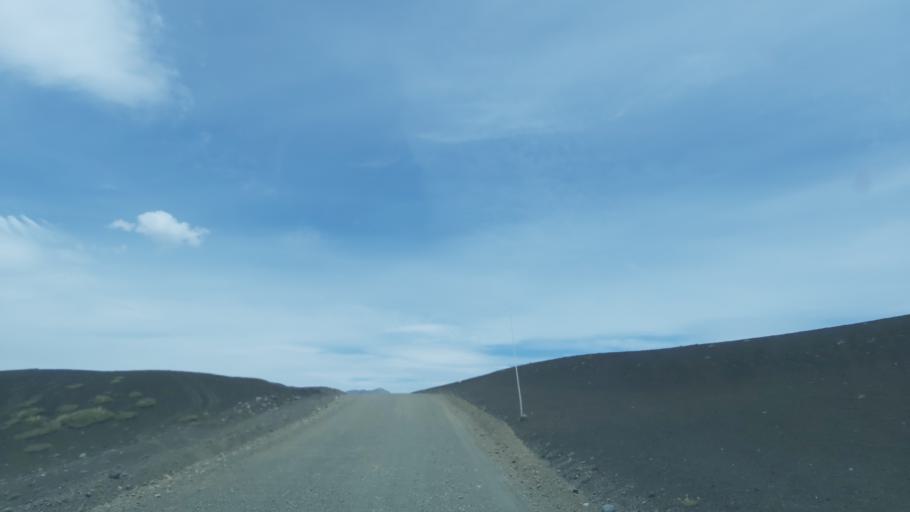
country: AR
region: Neuquen
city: Andacollo
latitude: -37.4134
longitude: -71.2917
